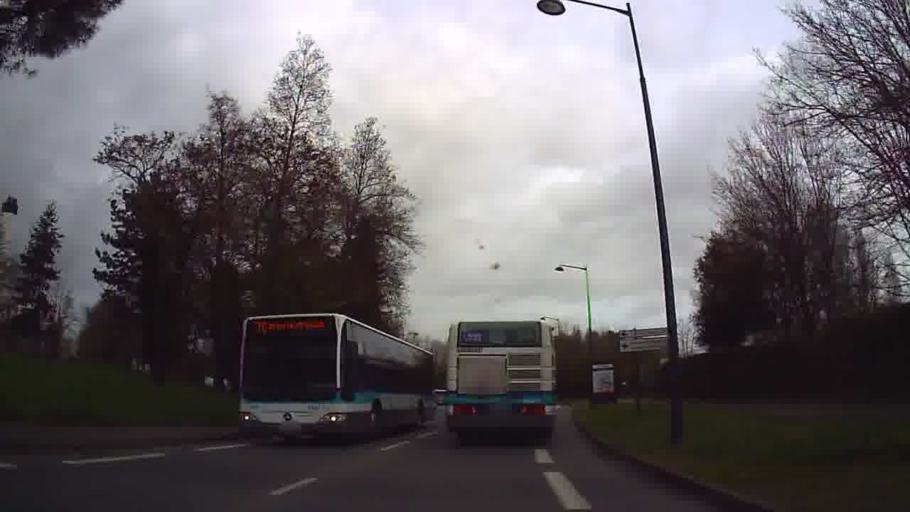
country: FR
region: Brittany
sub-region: Departement d'Ille-et-Vilaine
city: Rennes
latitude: 48.1238
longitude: -1.7036
